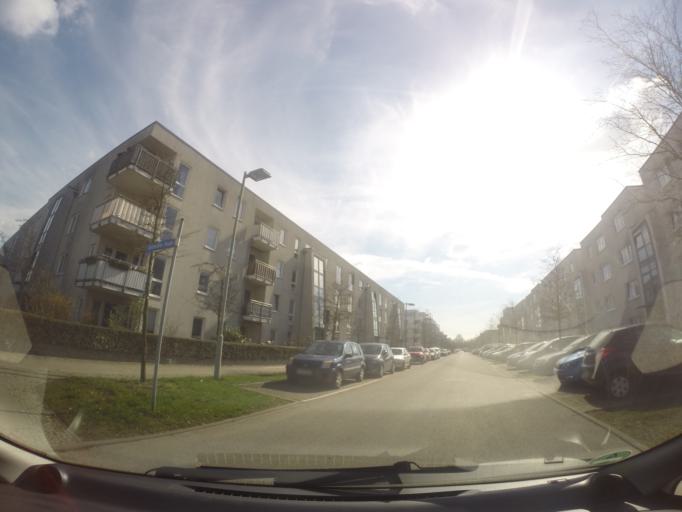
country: DE
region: Berlin
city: Marzahn
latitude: 52.5439
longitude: 13.5753
